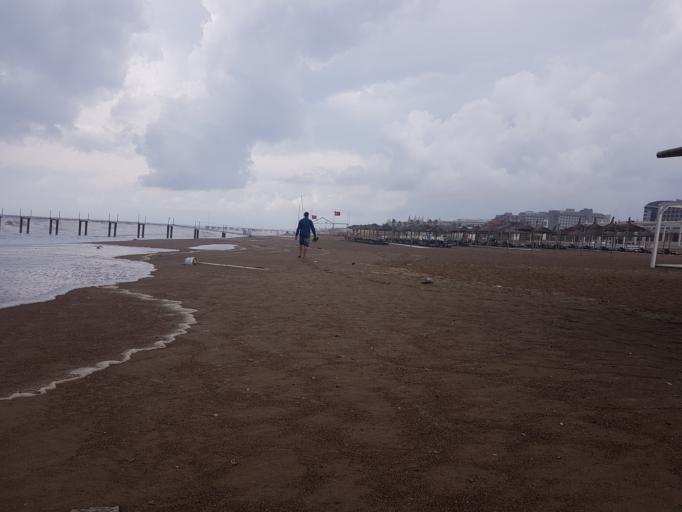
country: TR
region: Antalya
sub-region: Serik
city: Kumkoey
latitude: 36.8533
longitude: 30.8895
